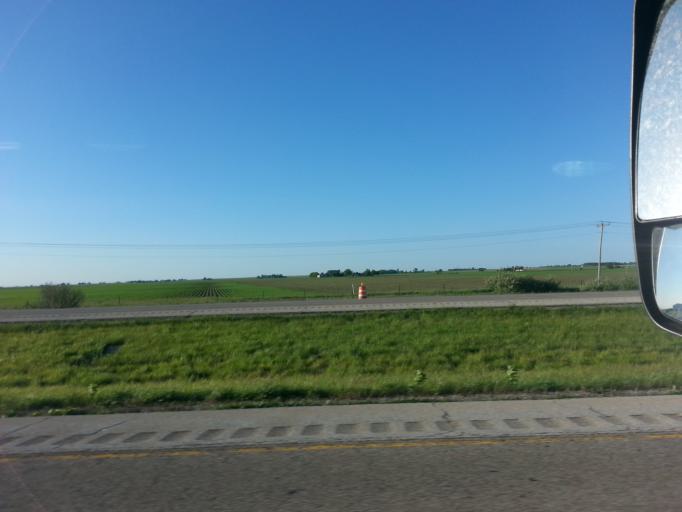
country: US
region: Illinois
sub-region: De Witt County
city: Farmer City
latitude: 40.2227
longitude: -88.5230
